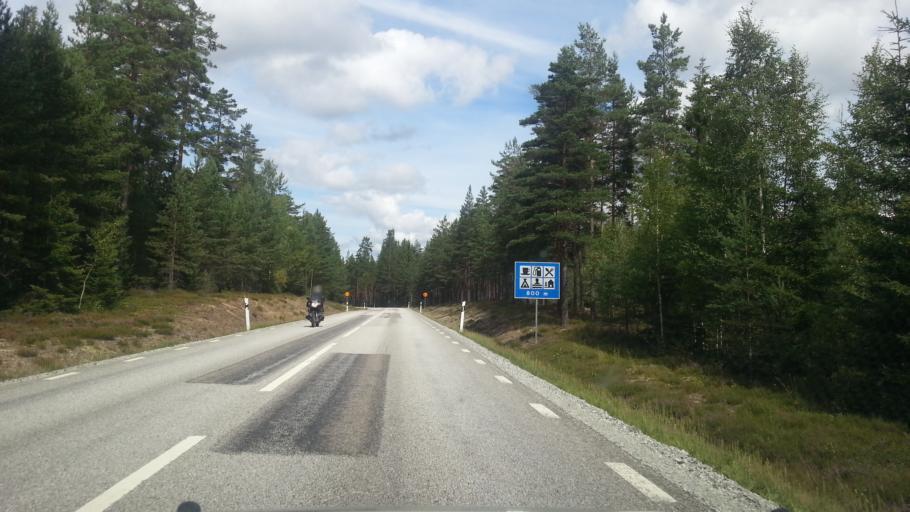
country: SE
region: Vaestmanland
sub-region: Skinnskattebergs Kommun
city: Skinnskatteberg
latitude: 59.8006
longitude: 15.5464
